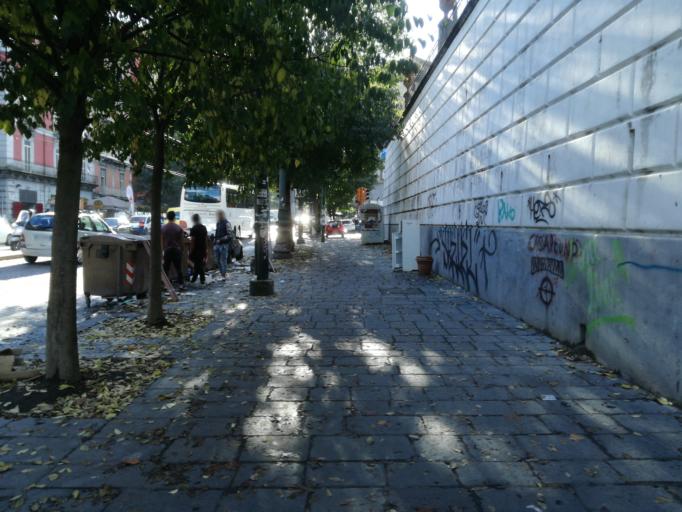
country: IT
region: Campania
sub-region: Provincia di Napoli
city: Napoli
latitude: 40.8601
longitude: 14.2627
